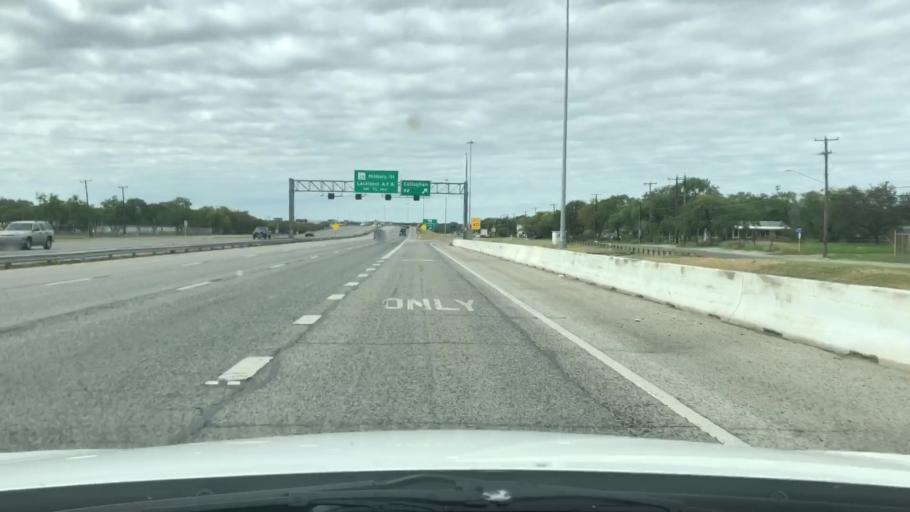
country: US
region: Texas
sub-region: Bexar County
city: Lackland Air Force Base
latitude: 29.4077
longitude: -98.5949
